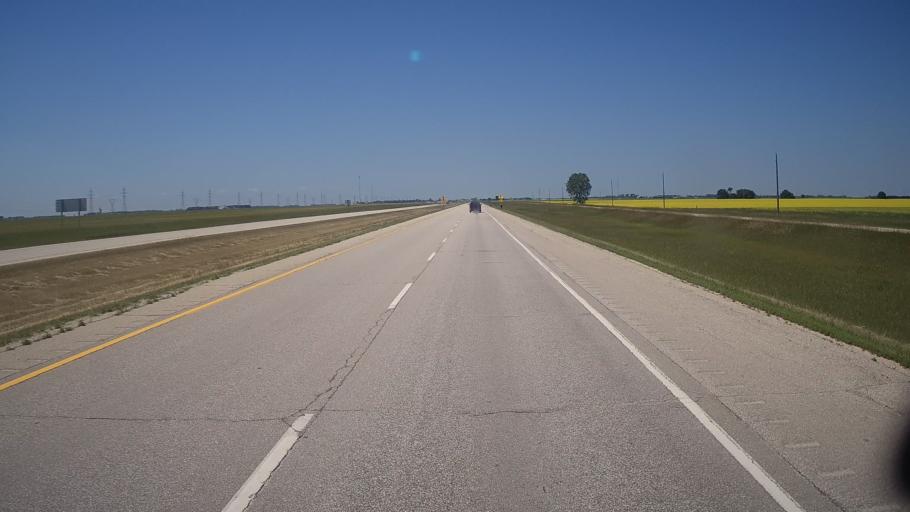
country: CA
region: Manitoba
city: Stonewall
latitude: 49.9901
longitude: -97.2773
